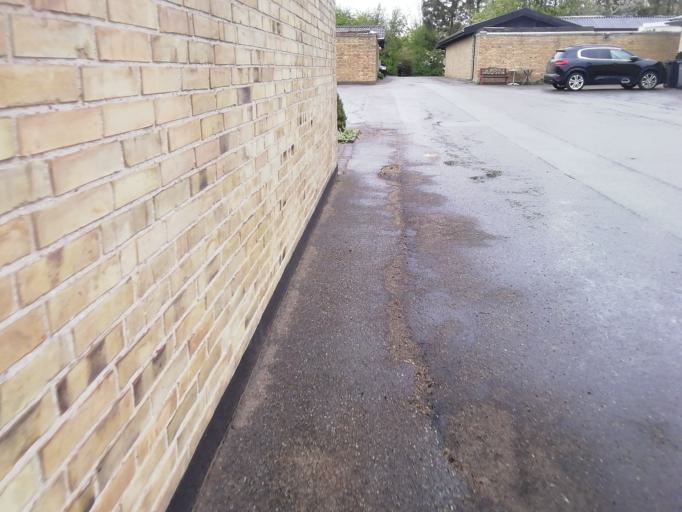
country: DK
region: Capital Region
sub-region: Egedal Kommune
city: Stenlose
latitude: 55.7701
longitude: 12.1705
